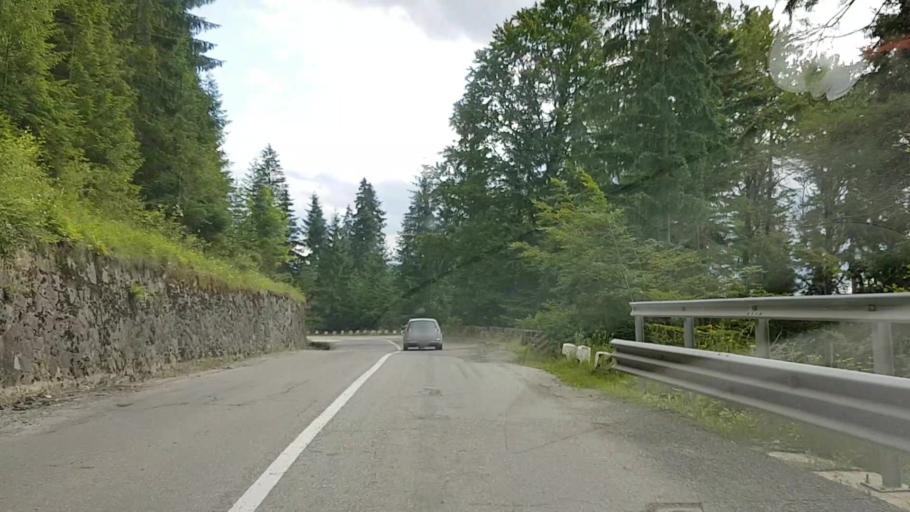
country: RO
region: Neamt
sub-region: Comuna Pangarati
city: Pangarati
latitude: 46.9742
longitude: 26.1166
